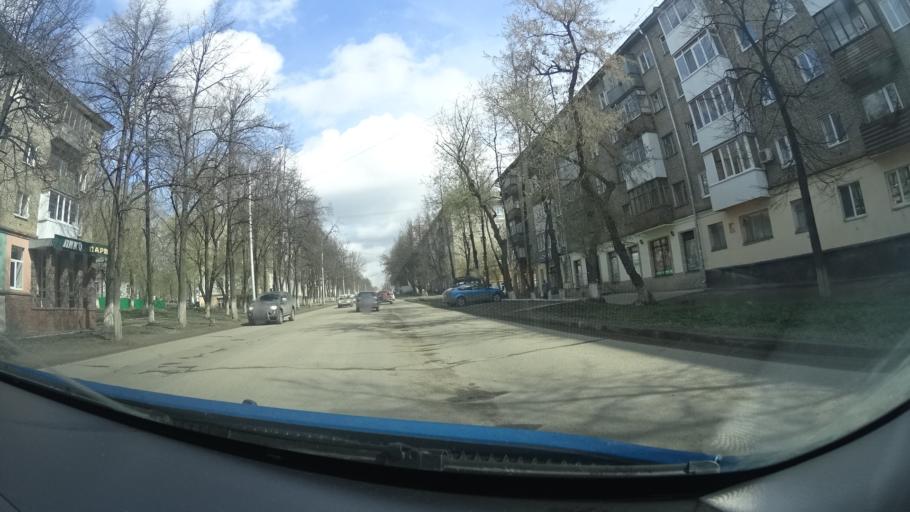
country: RU
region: Bashkortostan
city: Ufa
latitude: 54.8155
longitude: 56.0732
